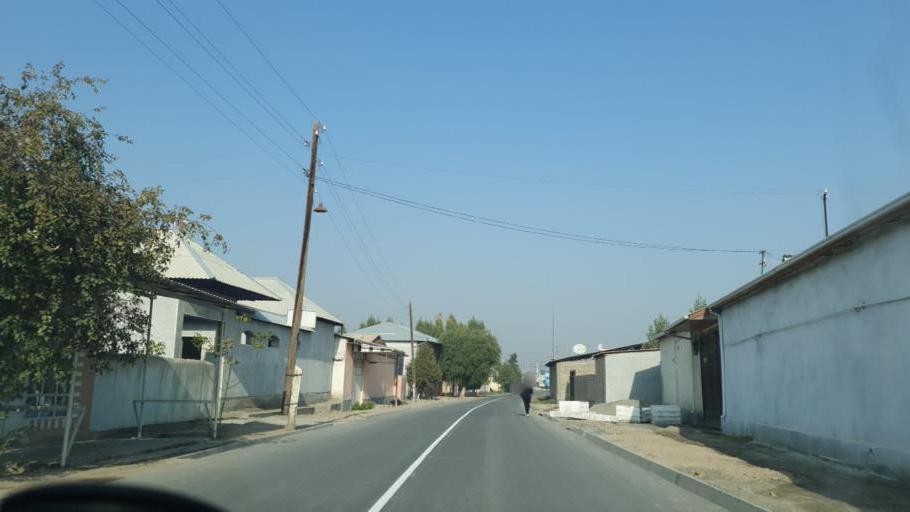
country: UZ
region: Fergana
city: Qo`qon
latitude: 40.5864
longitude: 70.9060
